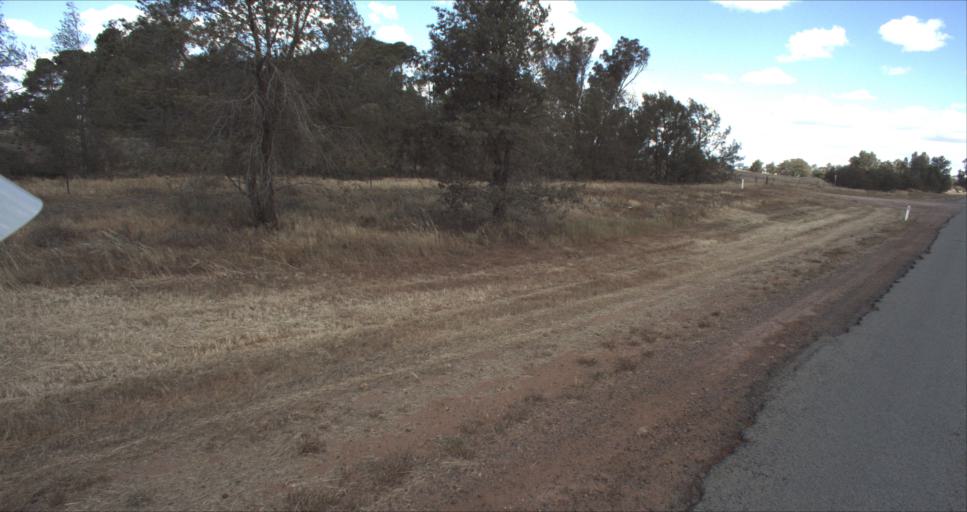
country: AU
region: New South Wales
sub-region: Leeton
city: Leeton
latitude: -34.4818
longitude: 146.2489
